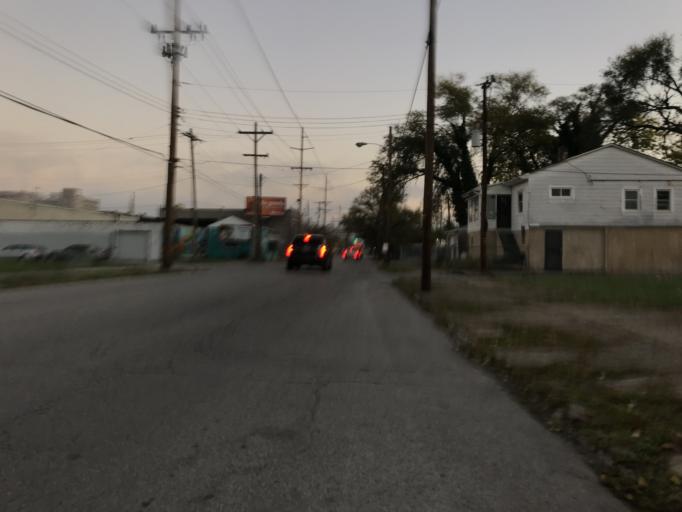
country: US
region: Kentucky
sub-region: Jefferson County
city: Louisville
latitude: 38.2434
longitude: -85.7418
